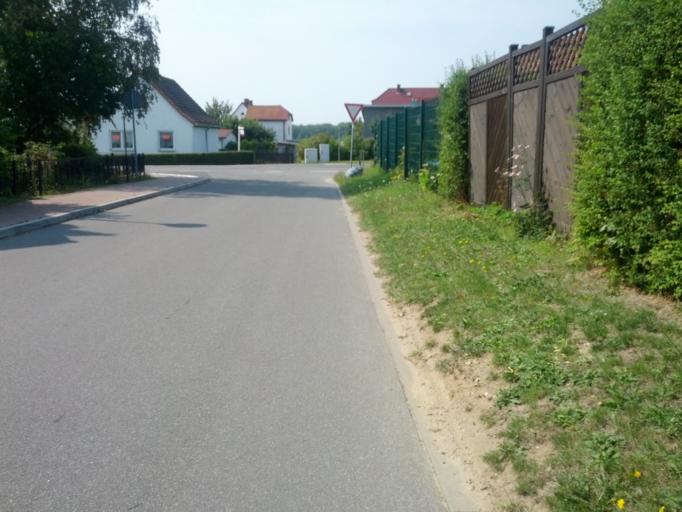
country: DE
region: Mecklenburg-Vorpommern
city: Bastorf
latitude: 54.1020
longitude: 11.6172
